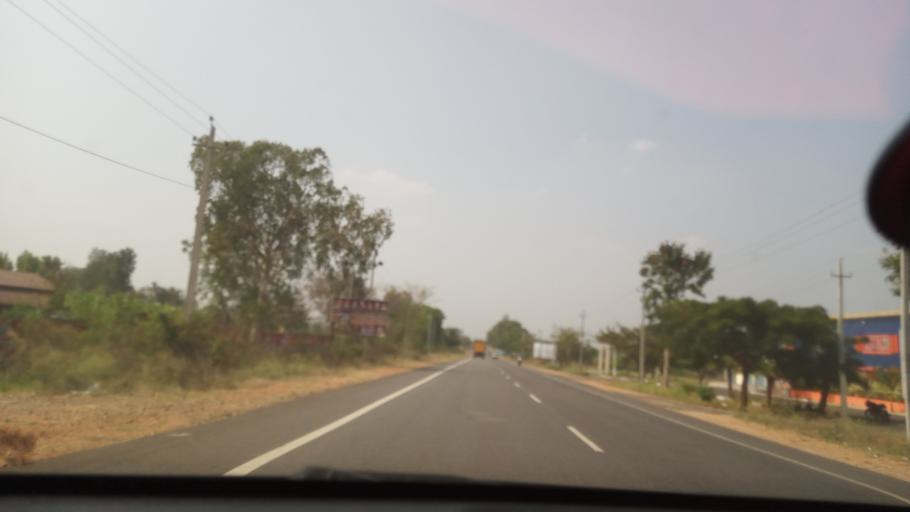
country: IN
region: Karnataka
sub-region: Mysore
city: Nanjangud
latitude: 12.0972
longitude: 76.7185
